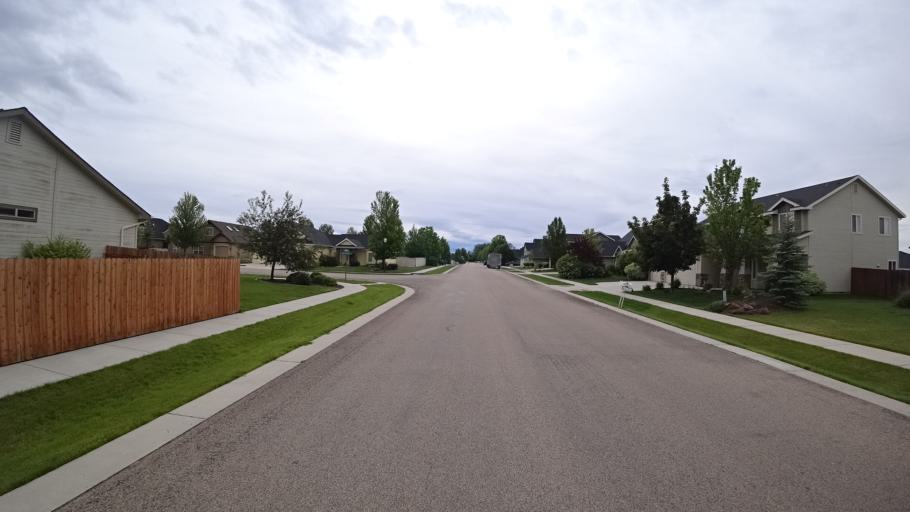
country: US
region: Idaho
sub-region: Ada County
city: Star
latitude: 43.6962
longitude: -116.5052
